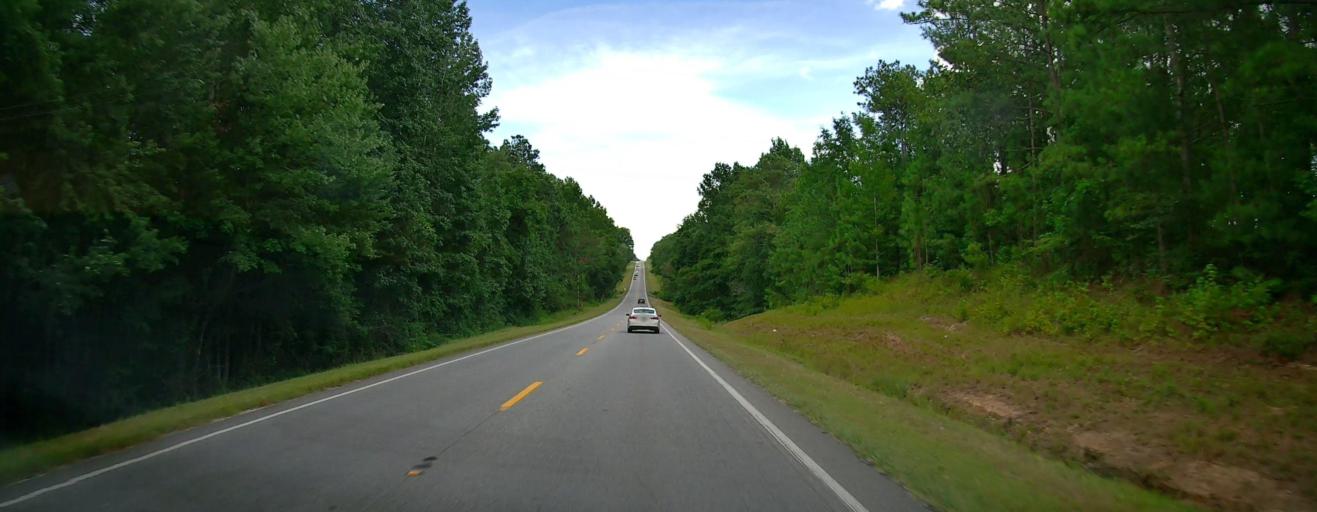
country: US
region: Alabama
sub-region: Russell County
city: Ladonia
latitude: 32.4514
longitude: -85.2155
